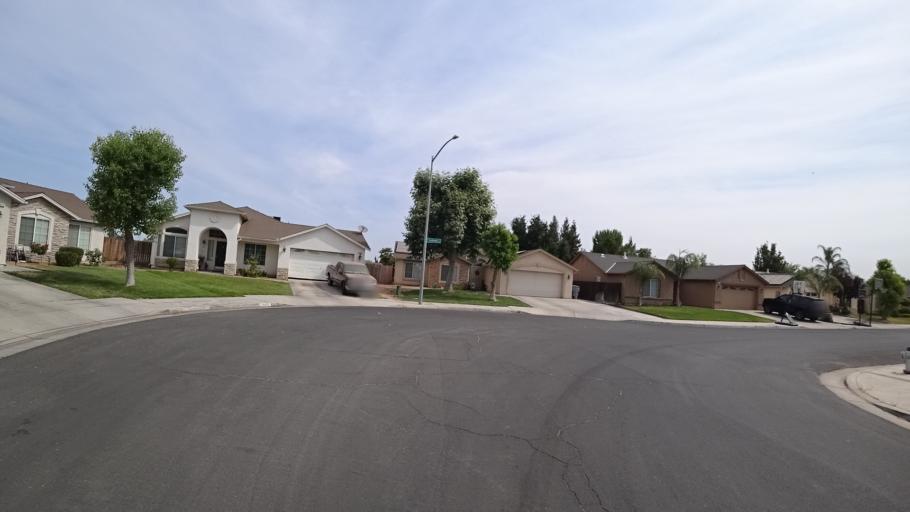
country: US
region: California
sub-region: Fresno County
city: West Park
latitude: 36.7597
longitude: -119.8932
